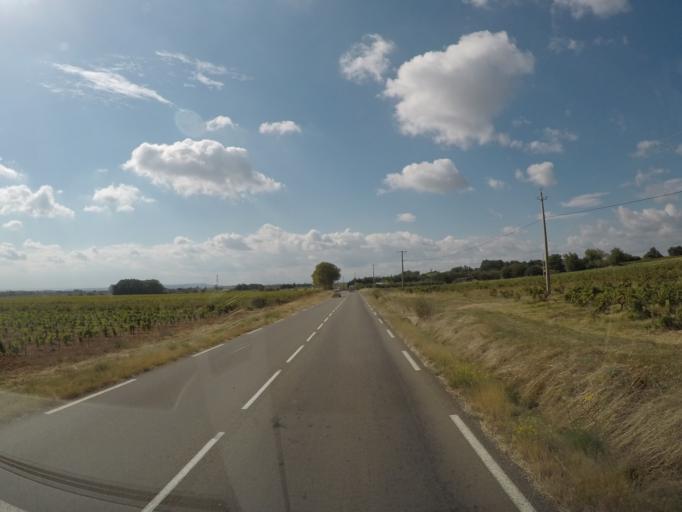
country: FR
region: Provence-Alpes-Cote d'Azur
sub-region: Departement du Vaucluse
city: Visan
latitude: 44.2897
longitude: 4.9605
